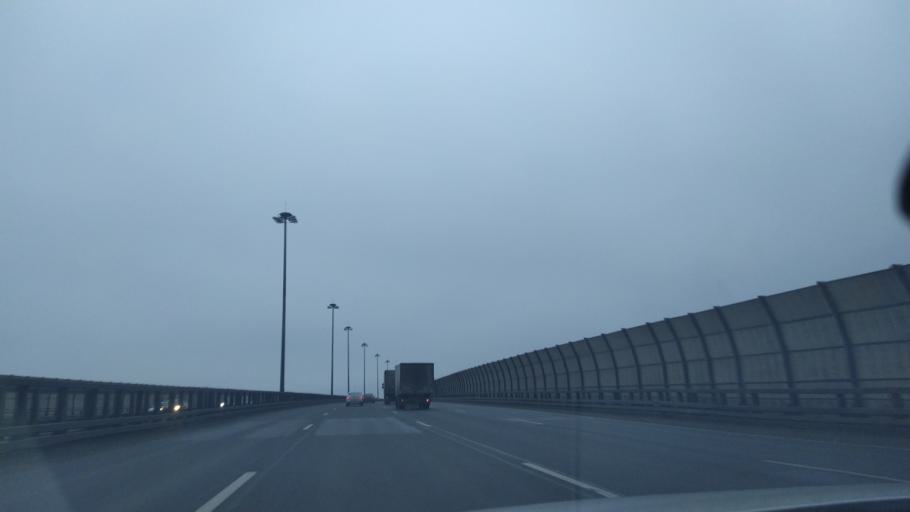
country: RU
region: St.-Petersburg
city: Krasnogvargeisky
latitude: 59.9816
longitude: 30.5143
